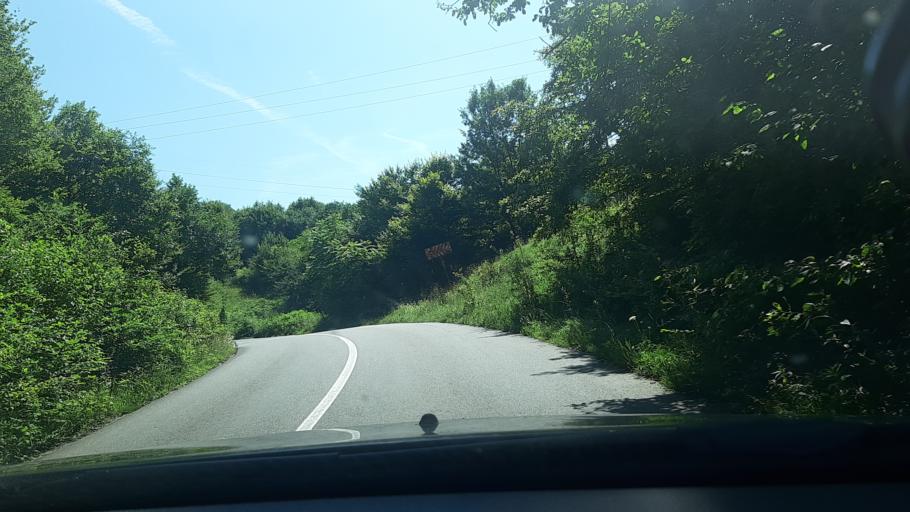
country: RO
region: Hunedoara
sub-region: Comuna Teliucu Inferior
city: Teliucu Inferior
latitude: 45.7013
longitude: 22.8815
